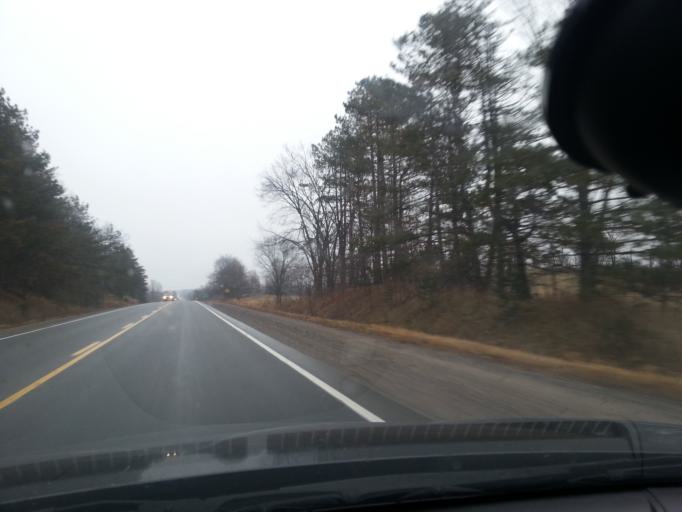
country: CA
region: Ontario
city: Belleville
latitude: 44.5208
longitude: -77.4347
